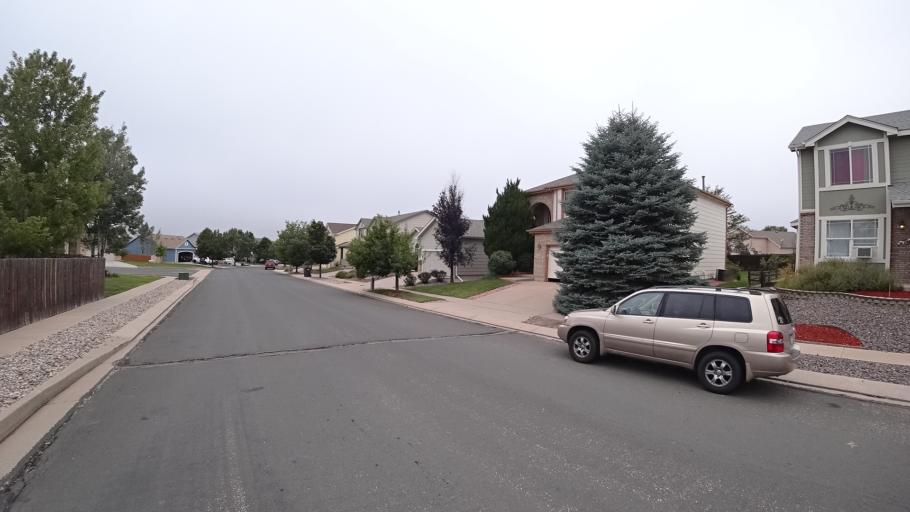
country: US
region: Colorado
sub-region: El Paso County
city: Cimarron Hills
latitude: 38.9324
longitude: -104.7464
